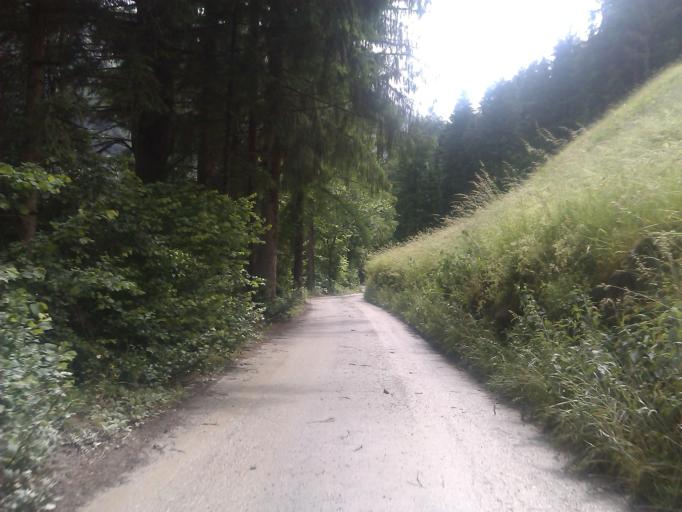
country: AT
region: Tyrol
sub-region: Politischer Bezirk Landeck
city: Prutz
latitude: 47.1127
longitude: 10.6435
